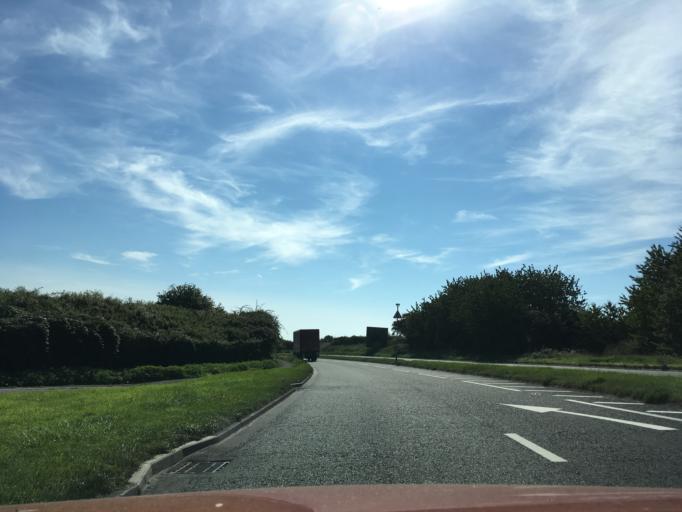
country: GB
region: England
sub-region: South Gloucestershire
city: Severn Beach
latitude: 51.5644
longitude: -2.6489
